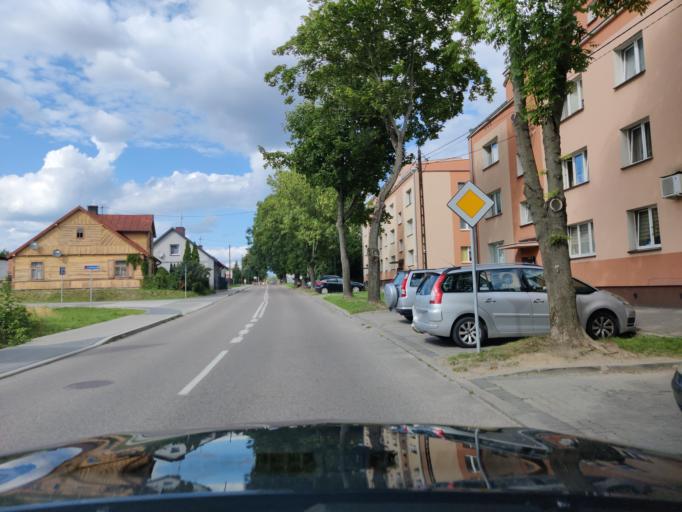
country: PL
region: Podlasie
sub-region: Powiat zambrowski
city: Zambrow
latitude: 52.9870
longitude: 22.2433
